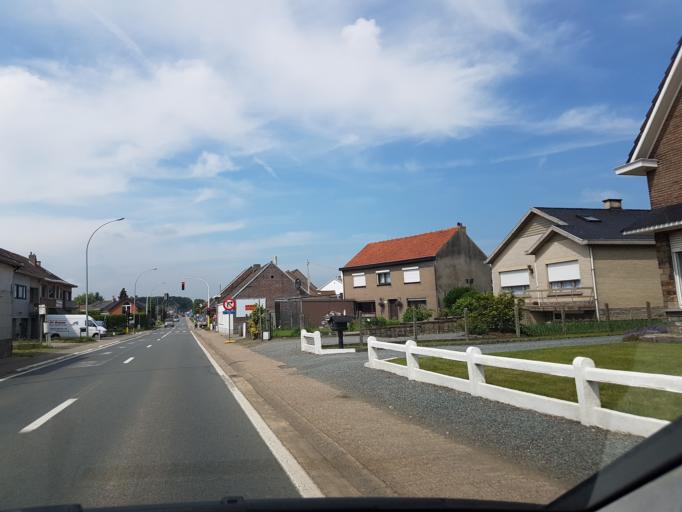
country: BE
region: Flanders
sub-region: Provincie Vlaams-Brabant
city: Opwijk
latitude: 50.9535
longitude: 4.1715
